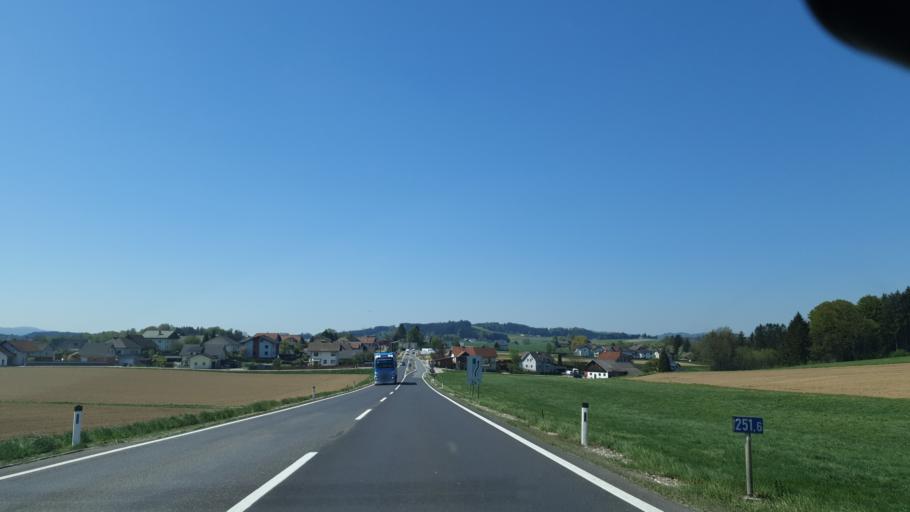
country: AT
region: Upper Austria
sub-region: Politischer Bezirk Vocklabruck
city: Gampern
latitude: 48.0011
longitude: 13.5736
